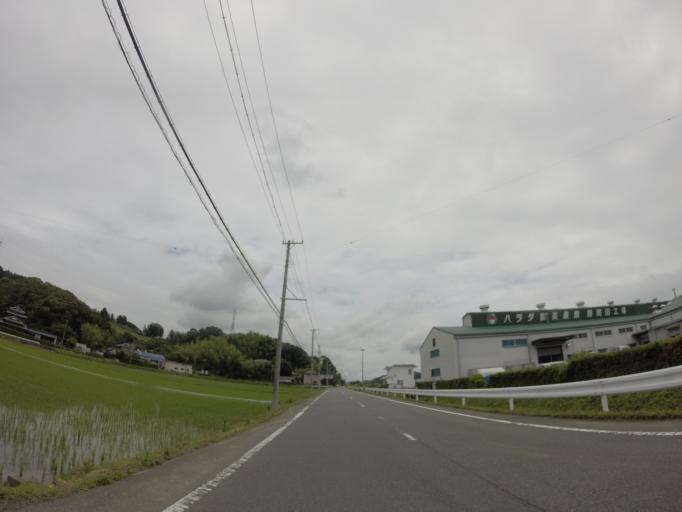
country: JP
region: Shizuoka
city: Shimada
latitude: 34.7742
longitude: 138.1781
